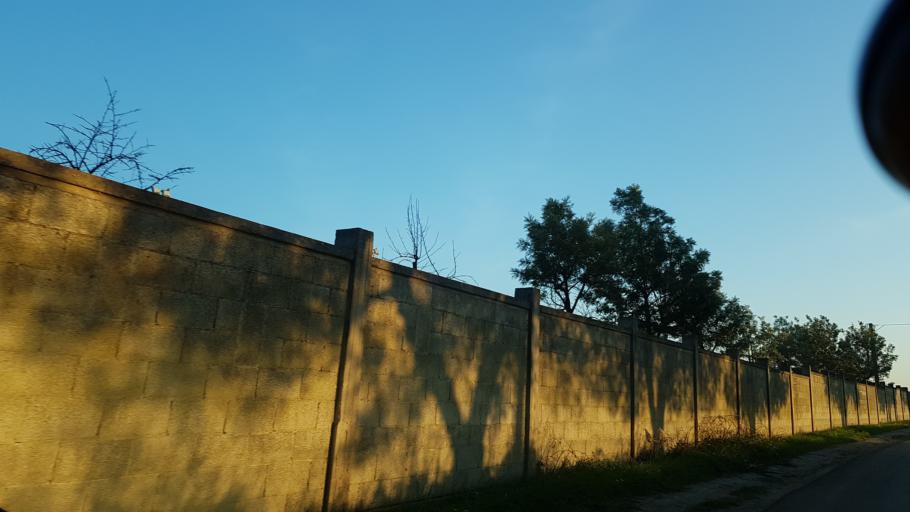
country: IT
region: Apulia
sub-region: Provincia di Brindisi
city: La Rosa
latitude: 40.6110
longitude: 17.9395
